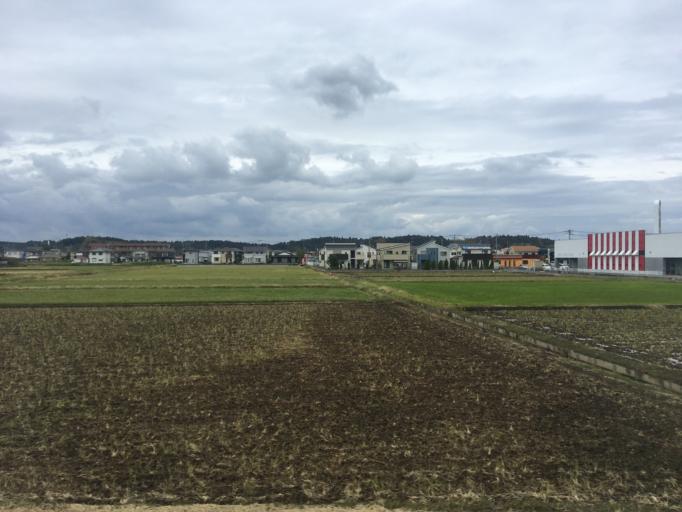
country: JP
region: Chiba
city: Togane
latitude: 35.5754
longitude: 140.3911
